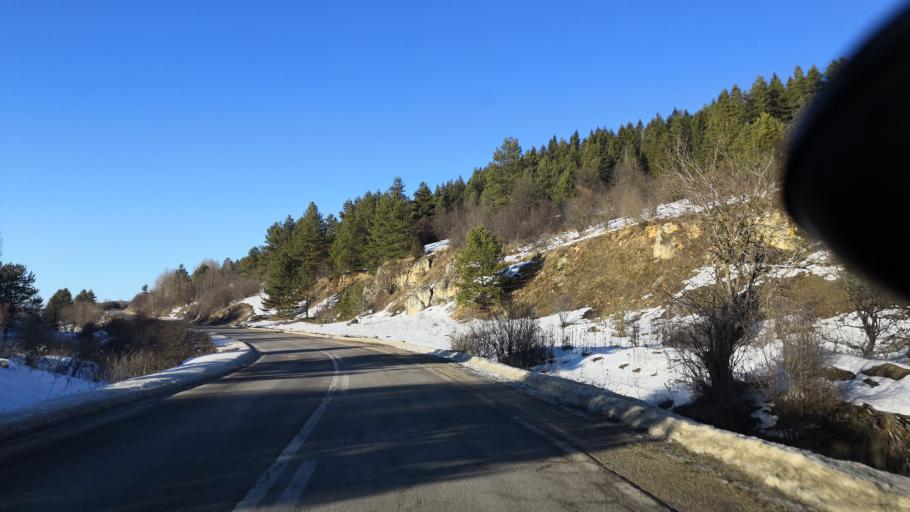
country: BA
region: Republika Srpska
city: Han Pijesak
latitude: 44.0090
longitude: 18.8903
